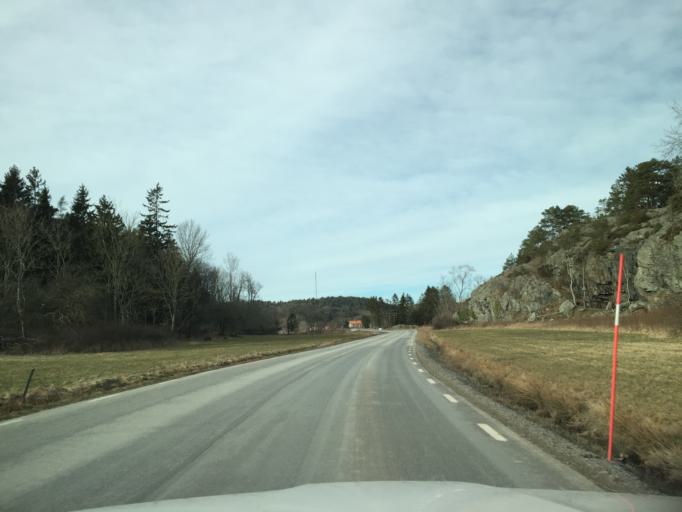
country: SE
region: Vaestra Goetaland
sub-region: Tjorns Kommun
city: Skaerhamn
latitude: 58.0312
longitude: 11.5948
